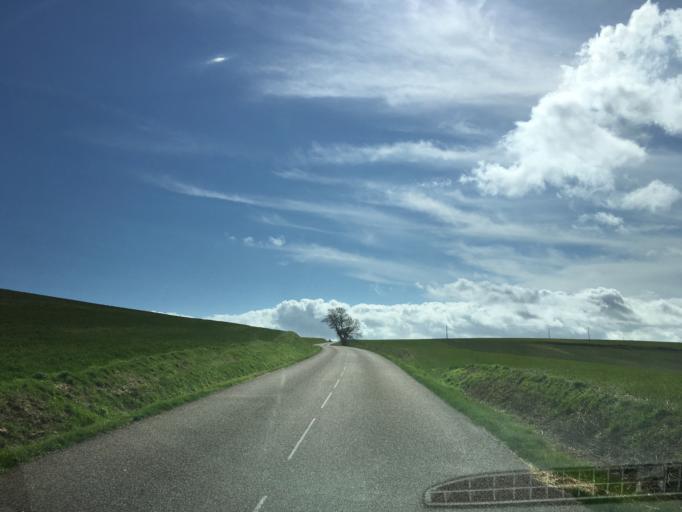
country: FR
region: Bourgogne
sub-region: Departement de l'Yonne
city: Pourrain
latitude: 47.7682
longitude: 3.4115
